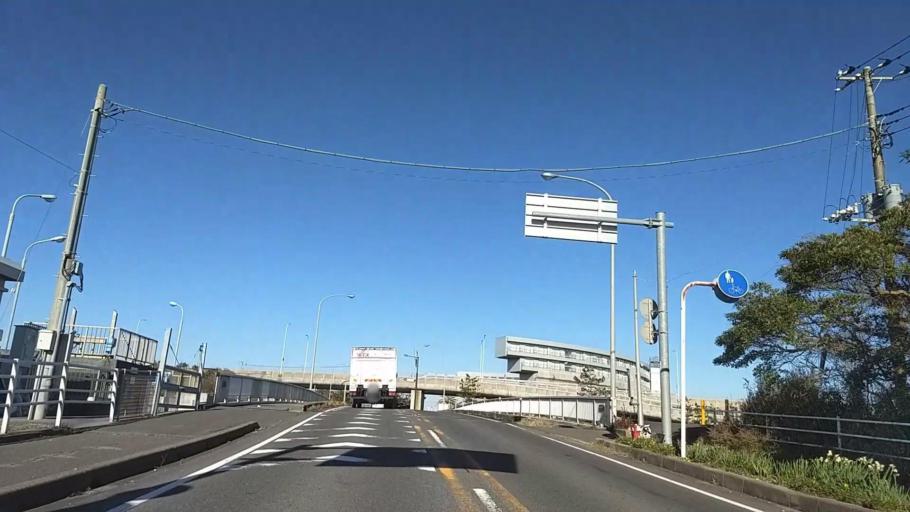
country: JP
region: Chiba
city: Togane
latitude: 35.4988
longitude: 140.4280
